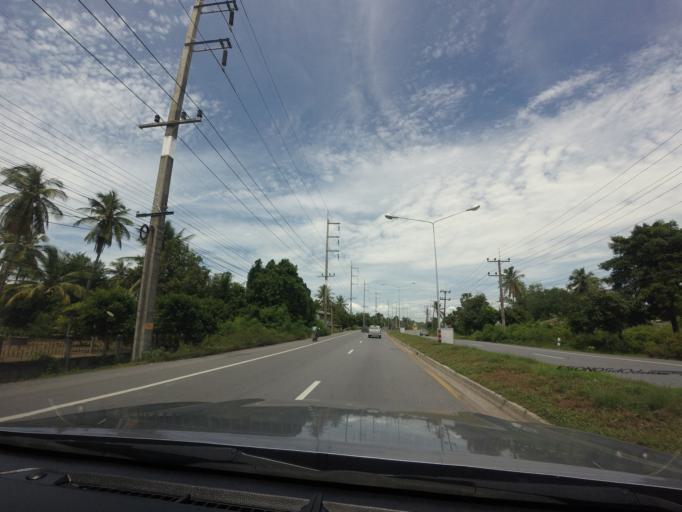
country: TH
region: Songkhla
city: Krasae Sin
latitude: 7.5971
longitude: 100.4027
